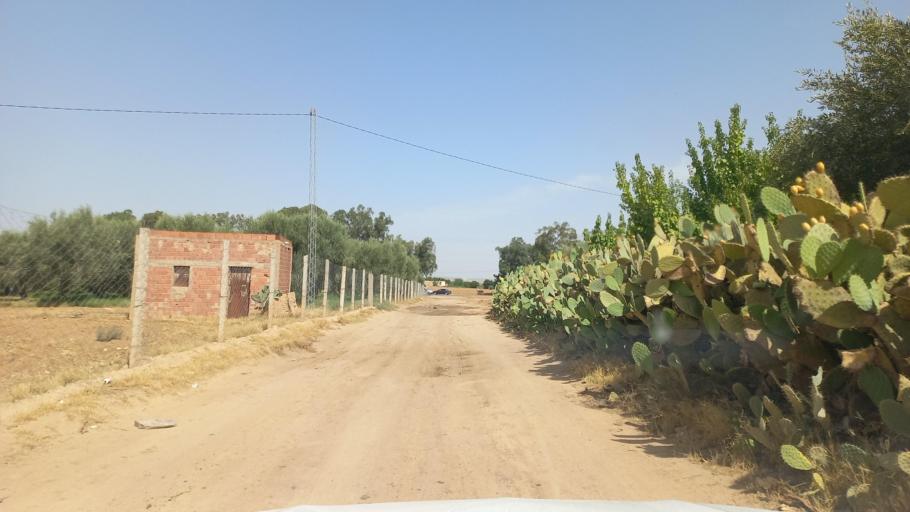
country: TN
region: Al Qasrayn
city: Kasserine
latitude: 35.2597
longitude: 9.0428
